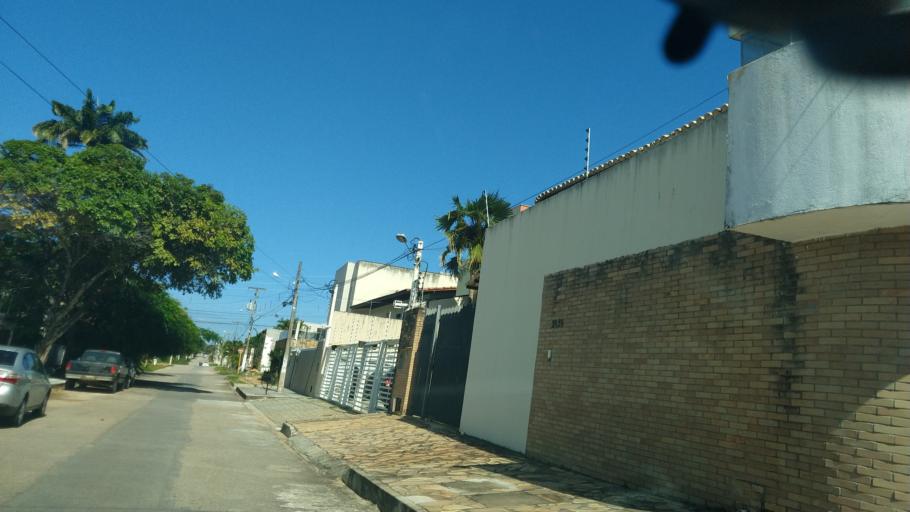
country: BR
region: Rio Grande do Norte
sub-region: Natal
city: Natal
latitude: -5.8455
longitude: -35.2044
